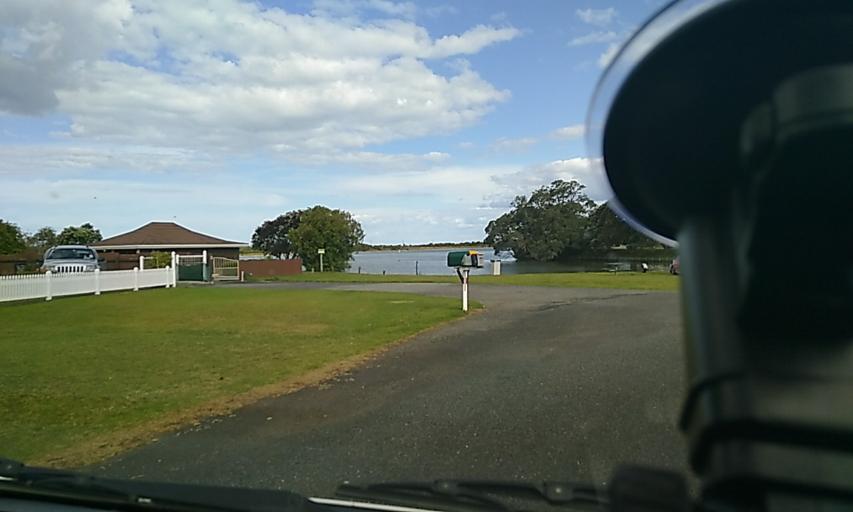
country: NZ
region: Bay of Plenty
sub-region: Western Bay of Plenty District
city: Waihi Beach
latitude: -37.4475
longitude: 175.9668
